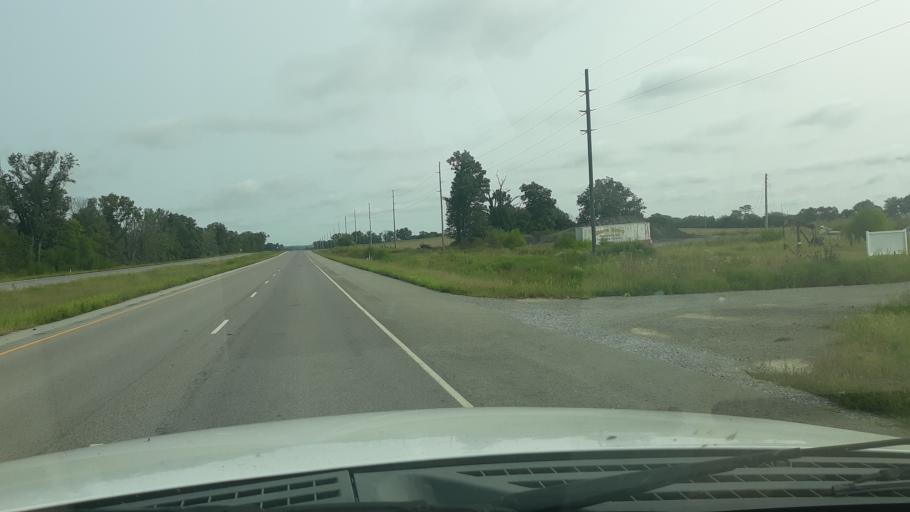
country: US
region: Illinois
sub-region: Saline County
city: Eldorado
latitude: 37.8369
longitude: -88.4177
